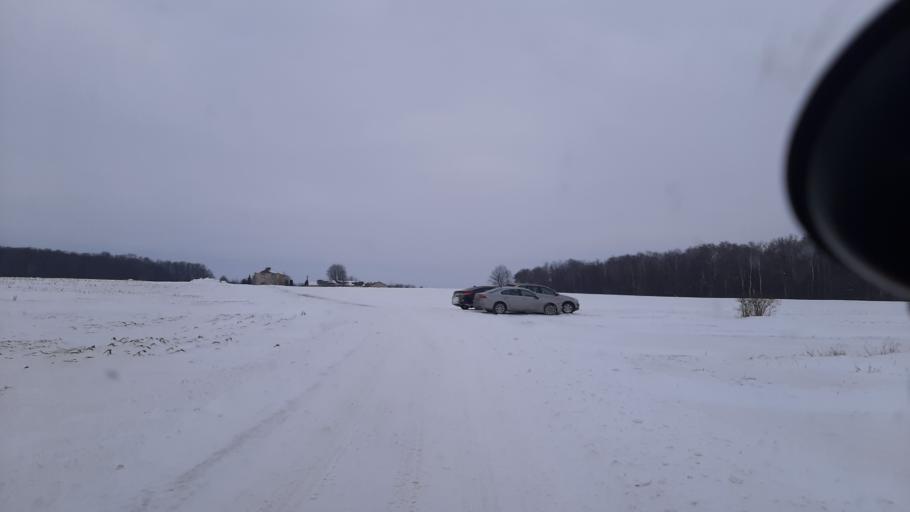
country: PL
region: Lublin Voivodeship
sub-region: Powiat lubelski
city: Garbow
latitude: 51.3274
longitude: 22.3094
